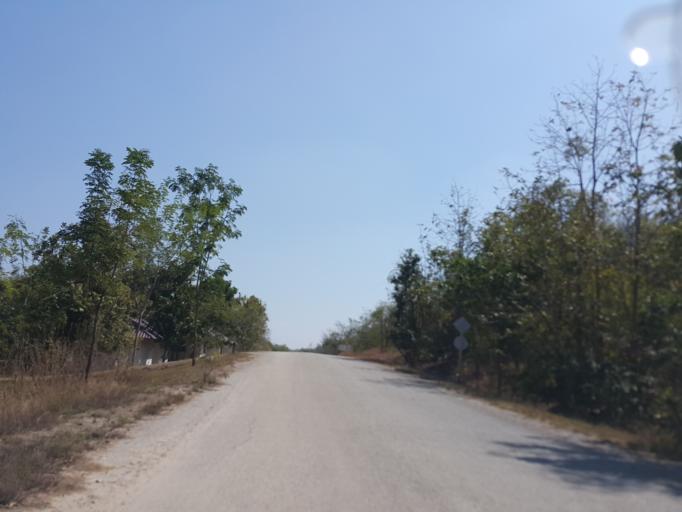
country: TH
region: Chiang Mai
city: Doi Lo
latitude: 18.5296
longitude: 98.7486
